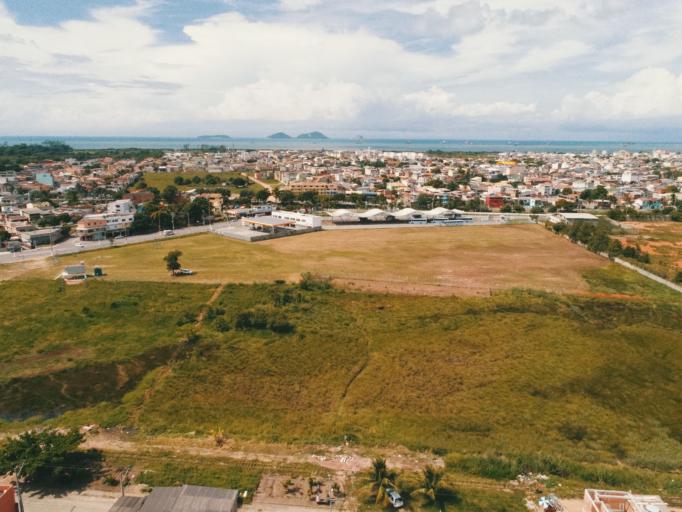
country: BR
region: Rio de Janeiro
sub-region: Macae
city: Macae
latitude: -22.3284
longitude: -41.7545
